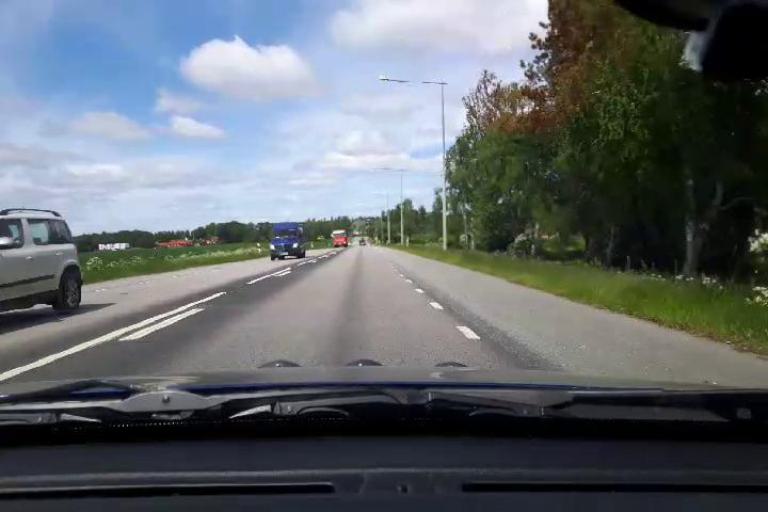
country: SE
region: Uppsala
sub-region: Osthammars Kommun
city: Bjorklinge
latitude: 60.0202
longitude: 17.5556
